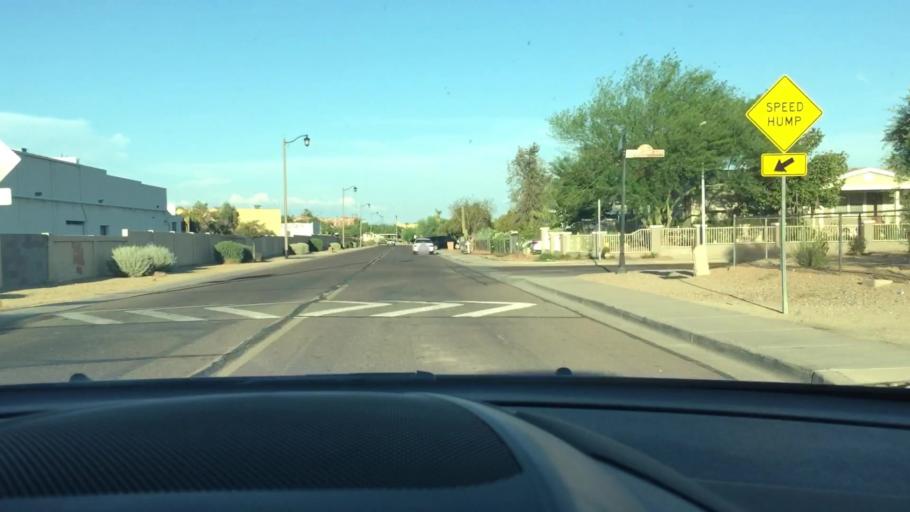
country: US
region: Arizona
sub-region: Maricopa County
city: Surprise
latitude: 33.6366
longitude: -112.3365
